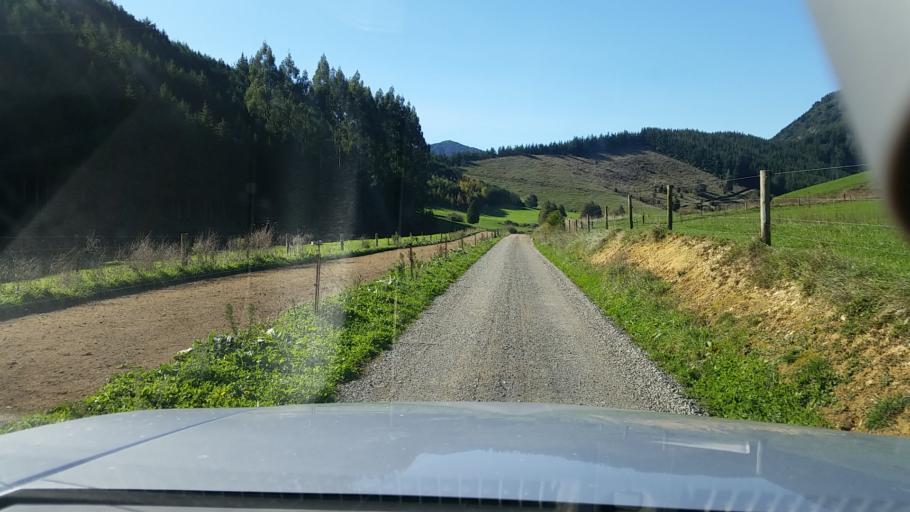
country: NZ
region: Nelson
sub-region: Nelson City
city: Nelson
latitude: -41.2228
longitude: 173.6043
